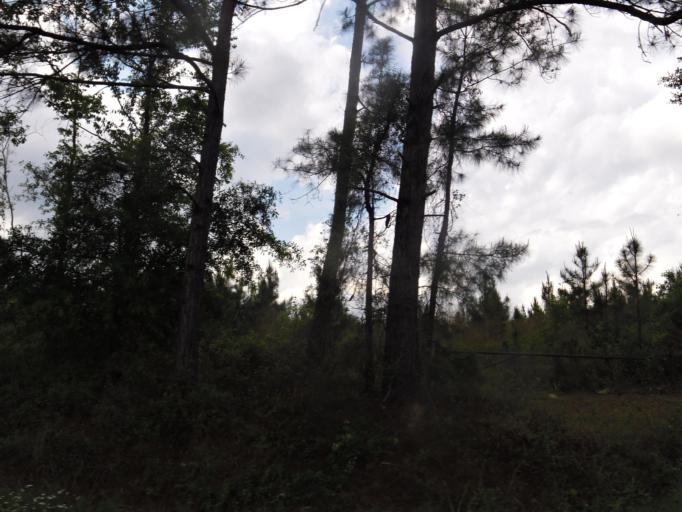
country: US
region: Georgia
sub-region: Charlton County
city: Folkston
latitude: 30.8248
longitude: -82.0415
